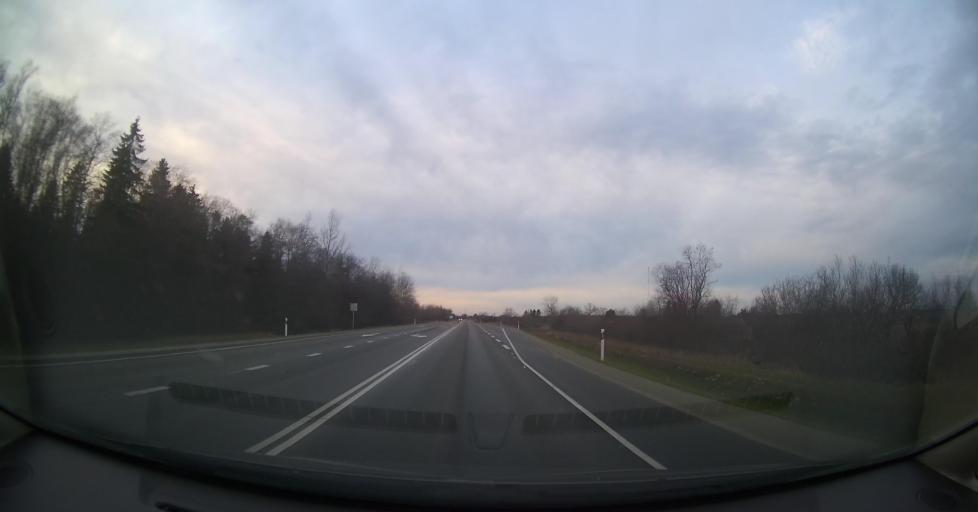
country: EE
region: Ida-Virumaa
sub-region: Kohtla-Jaerve linn
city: Kohtla-Jarve
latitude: 59.4207
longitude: 27.2169
